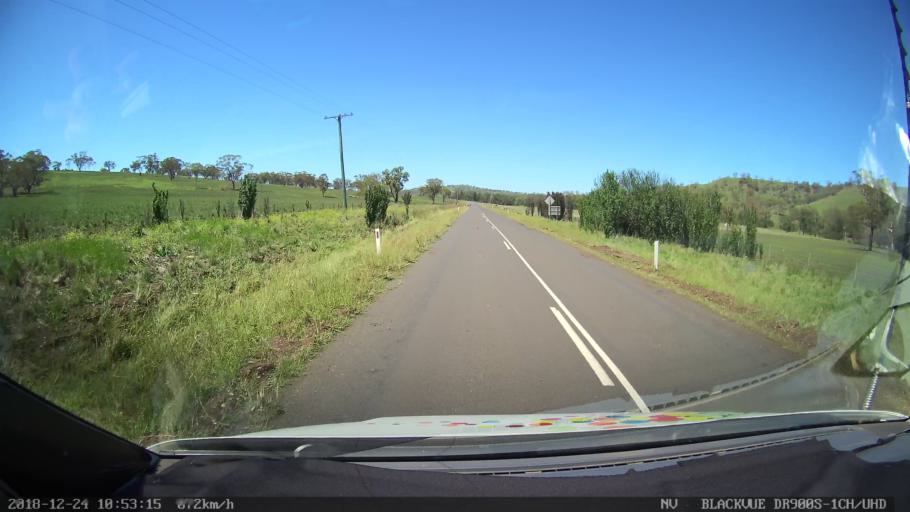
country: AU
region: New South Wales
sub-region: Upper Hunter Shire
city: Merriwa
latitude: -31.9896
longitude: 150.4222
